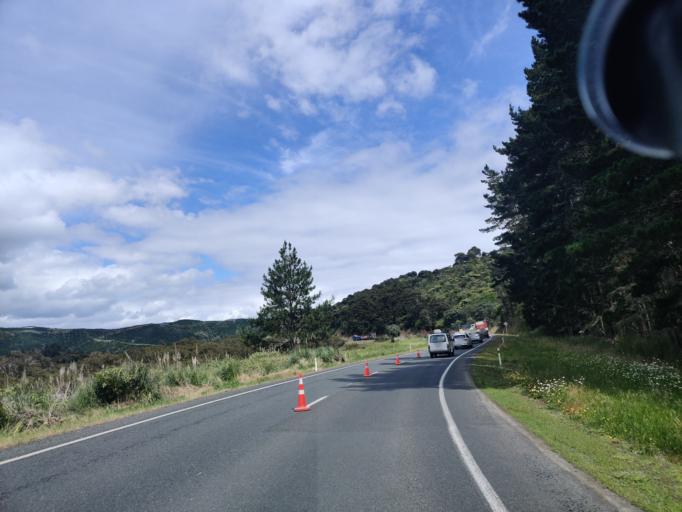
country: NZ
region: Northland
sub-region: Far North District
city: Taipa
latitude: -35.0120
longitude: 173.5532
